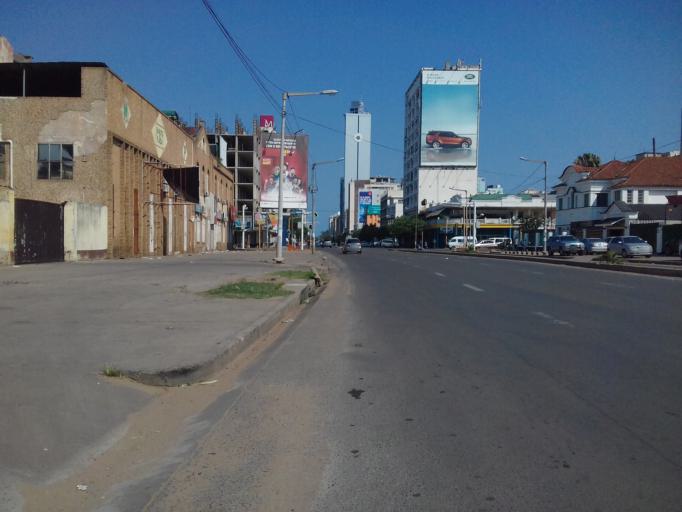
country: MZ
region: Maputo City
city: Maputo
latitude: -25.9695
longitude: 32.5655
